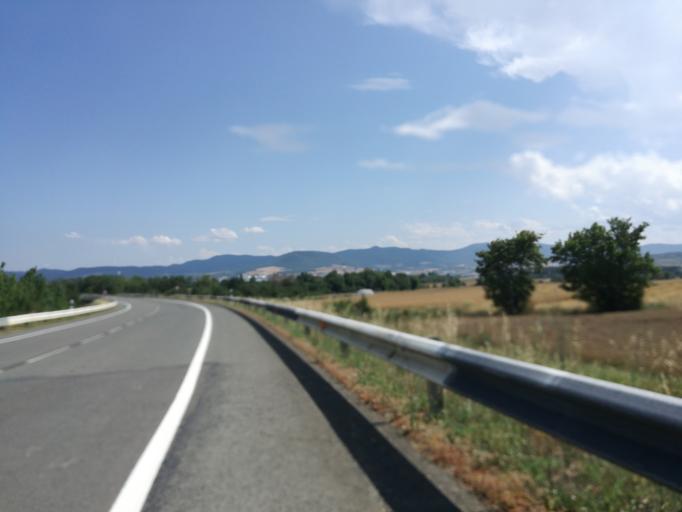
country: ES
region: Basque Country
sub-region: Provincia de Alava
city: Gasteiz / Vitoria
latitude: 42.8649
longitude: -2.7453
